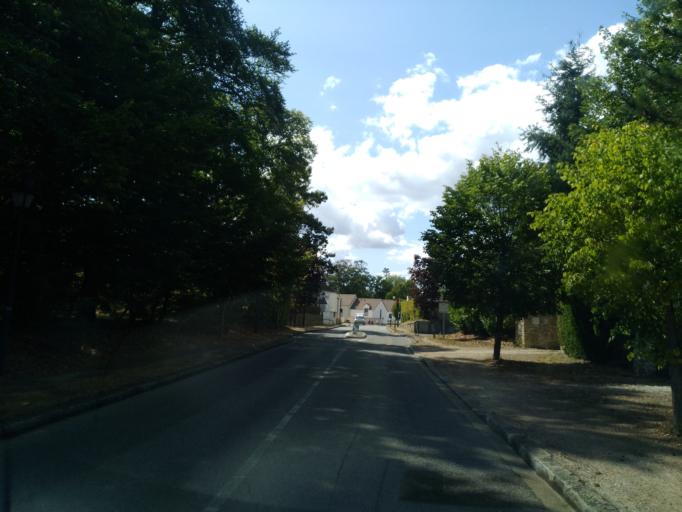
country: FR
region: Ile-de-France
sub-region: Departement des Yvelines
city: Sonchamp
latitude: 48.6122
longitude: 1.9110
